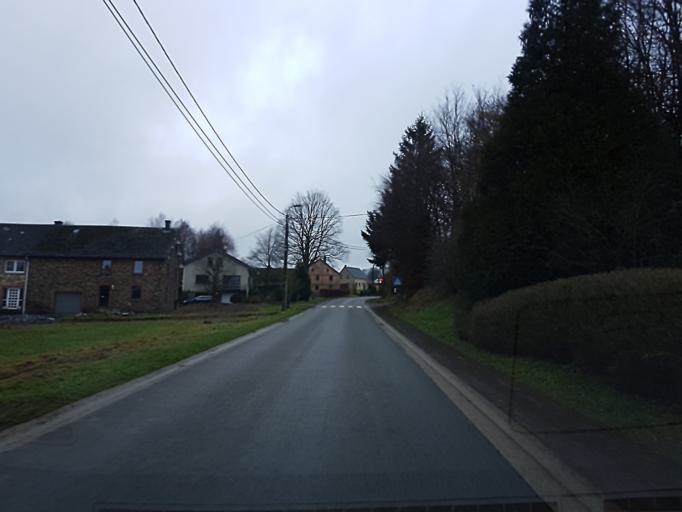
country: BE
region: Wallonia
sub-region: Province de Liege
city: Waimes
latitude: 50.4692
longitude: 6.0855
